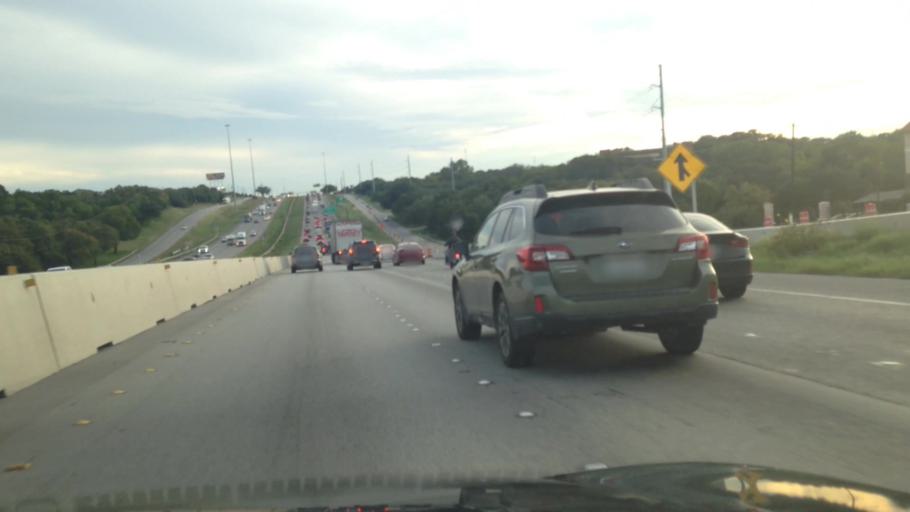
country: US
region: Texas
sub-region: Travis County
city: Onion Creek
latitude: 30.1816
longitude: -97.7767
